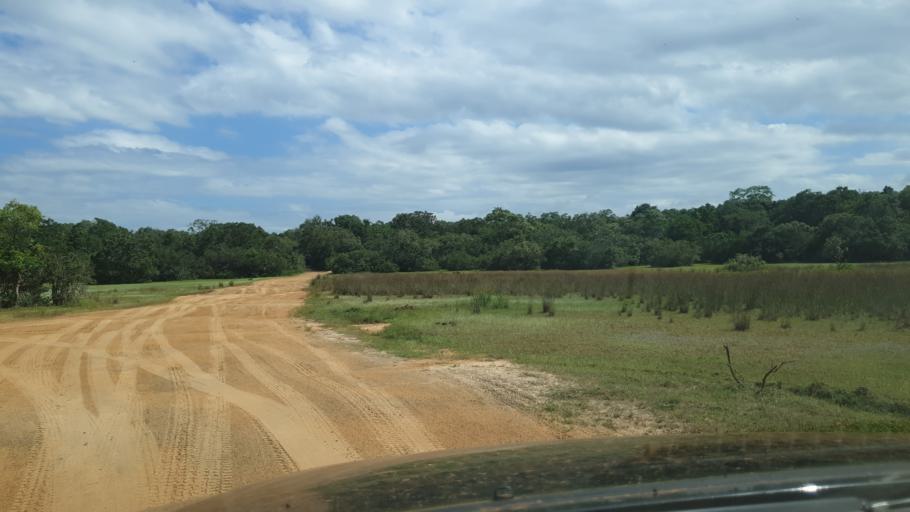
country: LK
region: North Central
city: Anuradhapura
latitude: 8.4212
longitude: 80.0099
